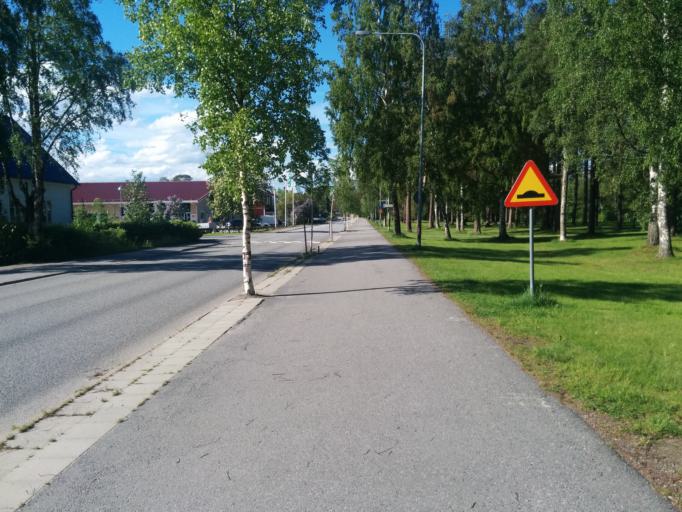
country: SE
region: Vaesterbotten
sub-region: Umea Kommun
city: Hoernefors
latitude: 63.6255
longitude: 19.9087
